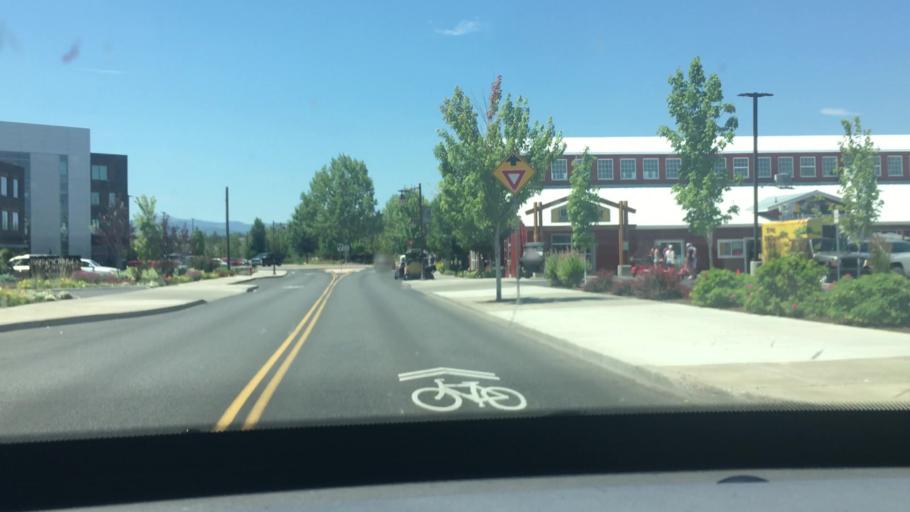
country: US
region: Oregon
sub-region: Deschutes County
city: Bend
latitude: 44.0504
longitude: -121.3149
